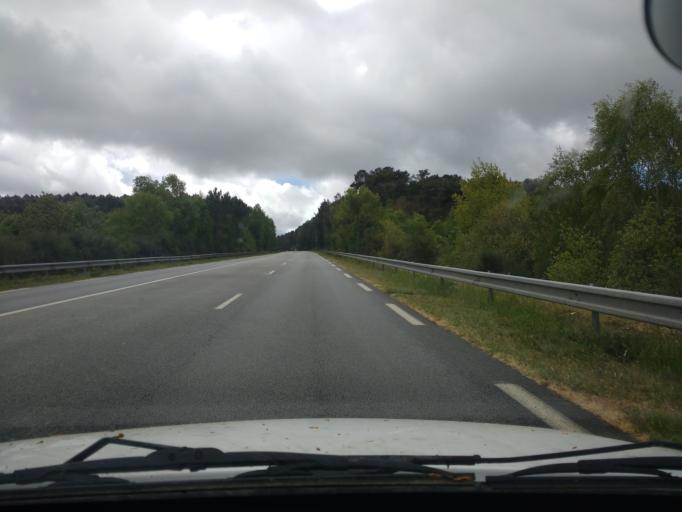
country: FR
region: Brittany
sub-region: Departement du Morbihan
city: Molac
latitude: 47.7135
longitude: -2.4423
